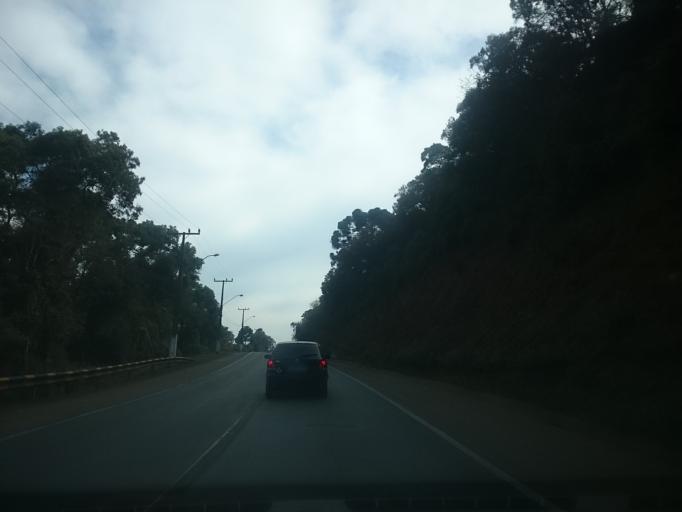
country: BR
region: Santa Catarina
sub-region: Lages
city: Lages
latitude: -27.8388
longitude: -50.3544
